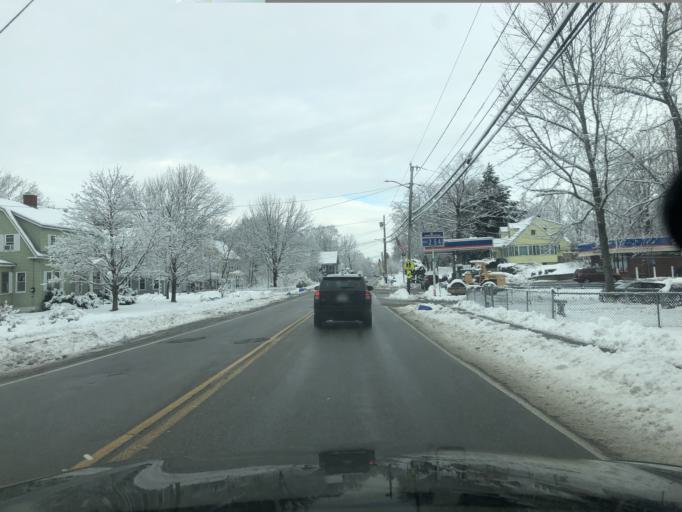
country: US
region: New Hampshire
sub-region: Strafford County
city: Somersworth
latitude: 43.2525
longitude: -70.8709
